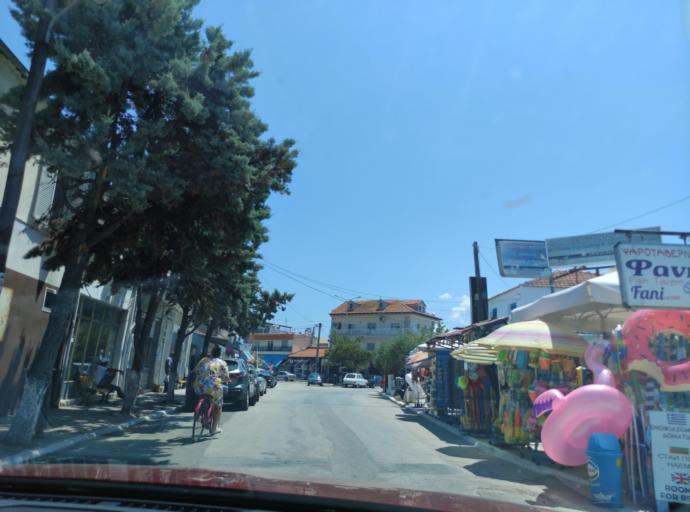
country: GR
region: East Macedonia and Thrace
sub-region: Nomos Kavalas
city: Keramoti
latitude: 40.8589
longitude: 24.7037
